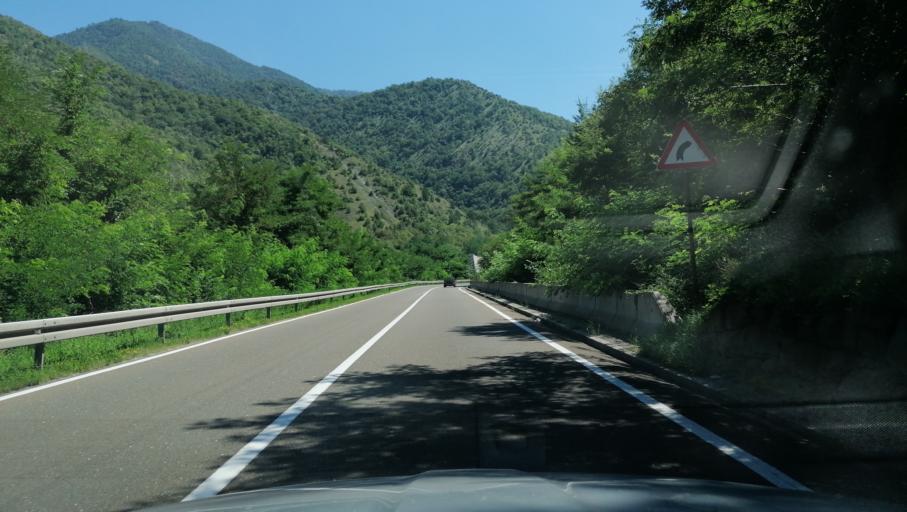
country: RS
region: Central Serbia
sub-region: Raski Okrug
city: Kraljevo
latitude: 43.5954
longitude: 20.5681
